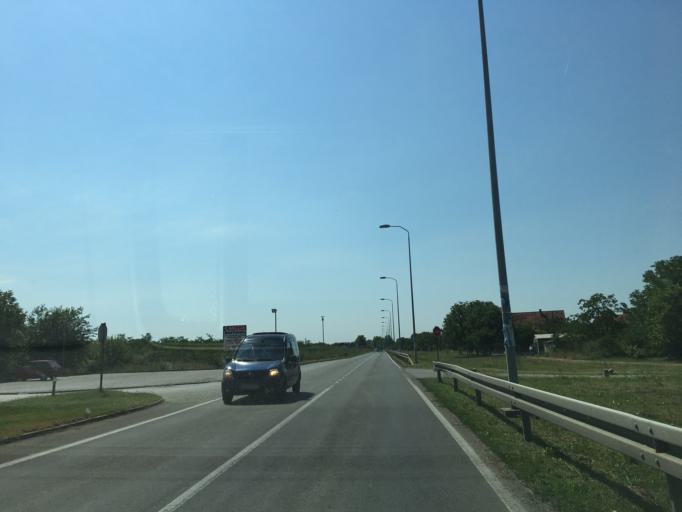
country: RS
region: Autonomna Pokrajina Vojvodina
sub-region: Juznobanatski Okrug
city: Pancevo
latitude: 44.8207
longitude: 20.6913
